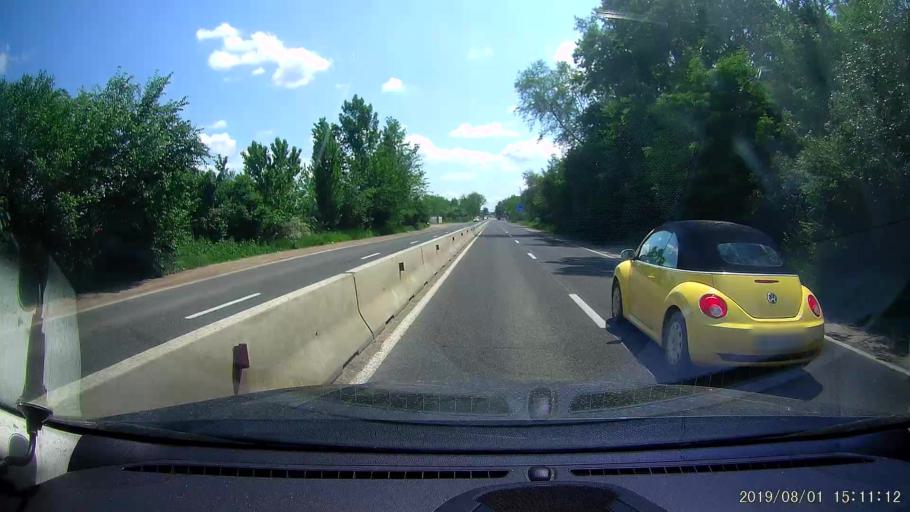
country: RO
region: Braila
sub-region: Comuna Chiscani
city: Chiscani
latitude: 45.2197
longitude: 27.9260
